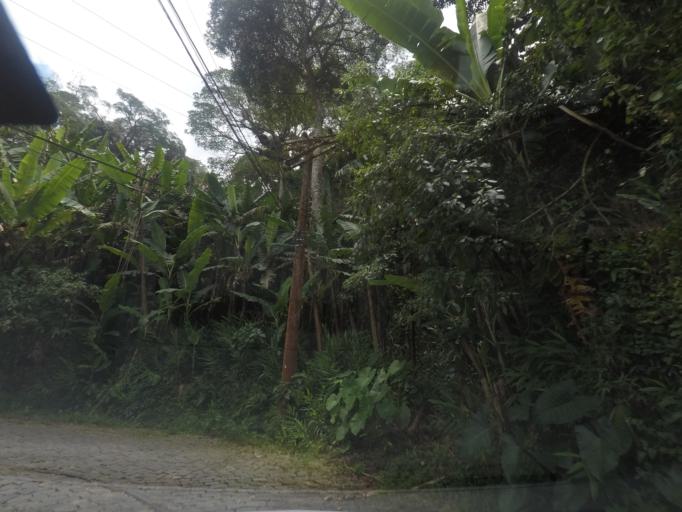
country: BR
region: Rio de Janeiro
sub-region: Petropolis
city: Petropolis
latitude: -22.4998
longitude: -43.1872
